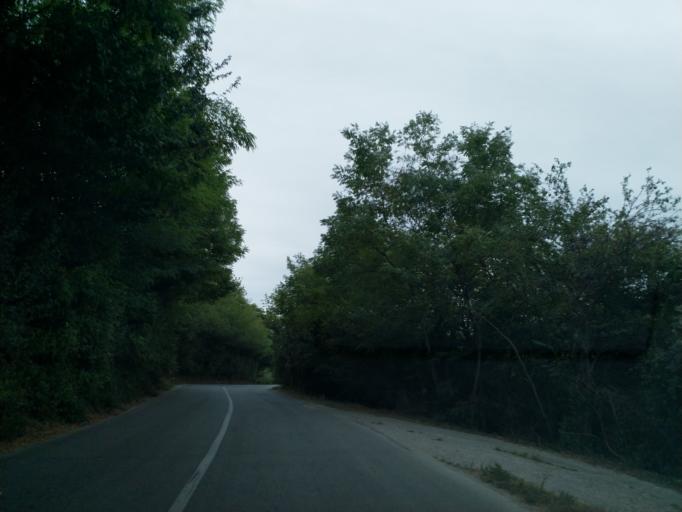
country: RS
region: Central Serbia
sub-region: Pomoravski Okrug
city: Jagodina
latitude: 44.0465
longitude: 21.1836
